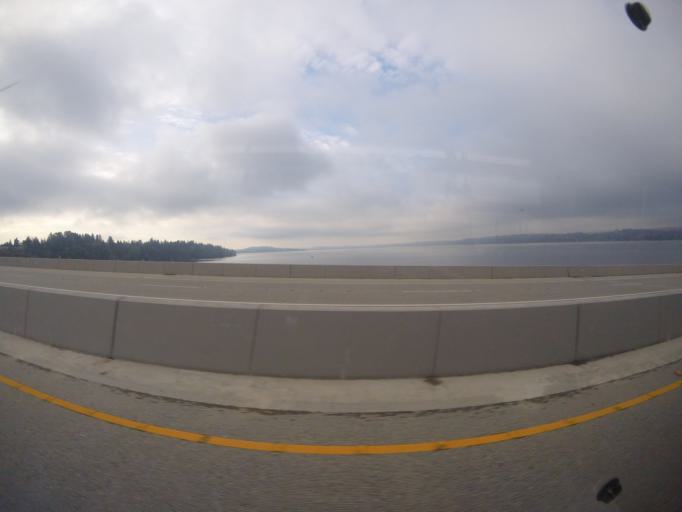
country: US
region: Washington
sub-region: King County
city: Medina
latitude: 47.6388
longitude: -122.2454
